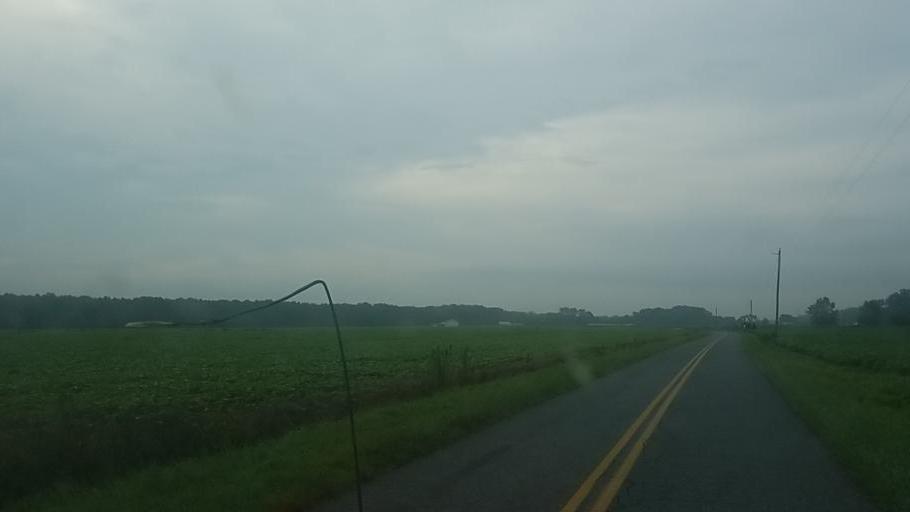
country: US
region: Maryland
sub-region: Wicomico County
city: Pittsville
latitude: 38.4261
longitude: -75.3212
